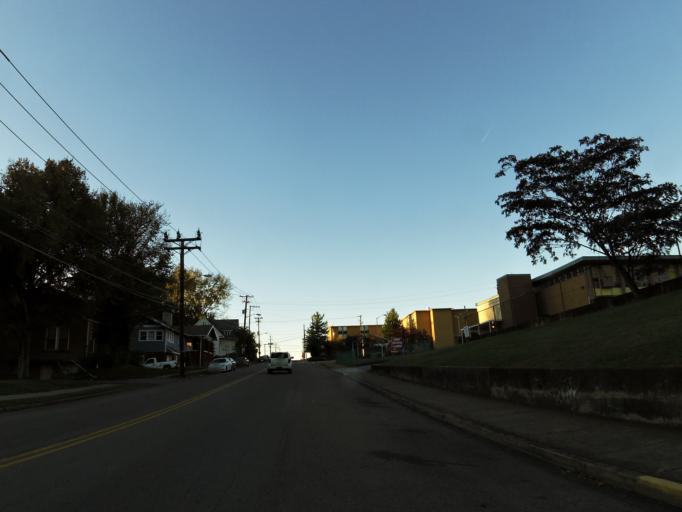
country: US
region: Tennessee
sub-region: Knox County
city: Knoxville
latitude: 35.9558
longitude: -83.9400
